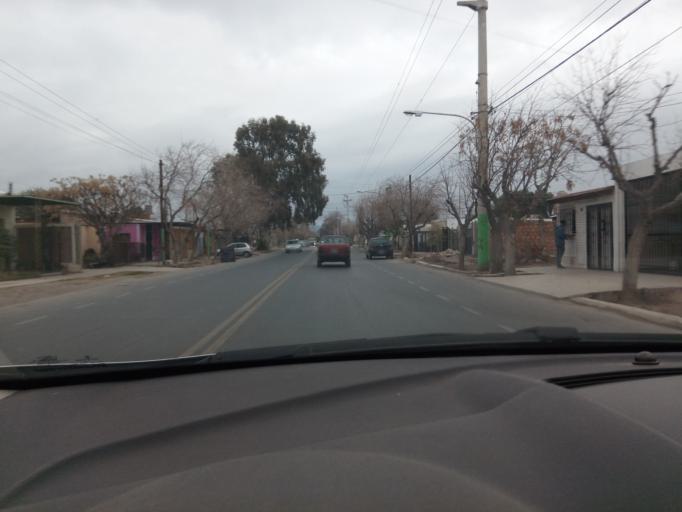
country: AR
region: San Juan
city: San Juan
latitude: -31.5506
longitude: -68.5672
